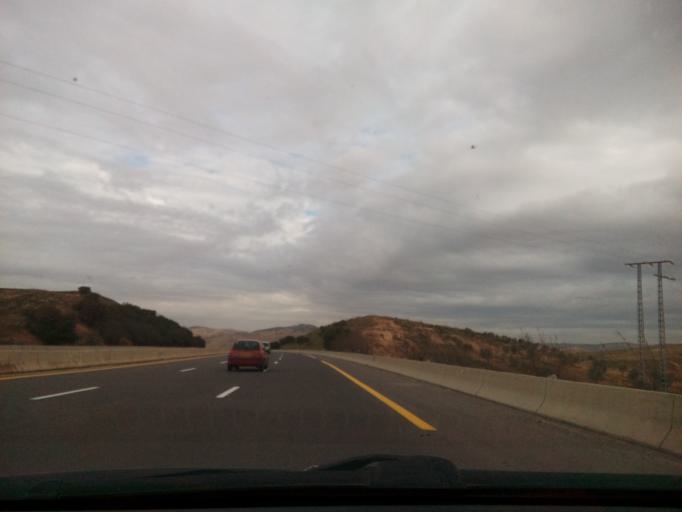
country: DZ
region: Sidi Bel Abbes
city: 'Ain el Berd
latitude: 35.4462
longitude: -0.4023
